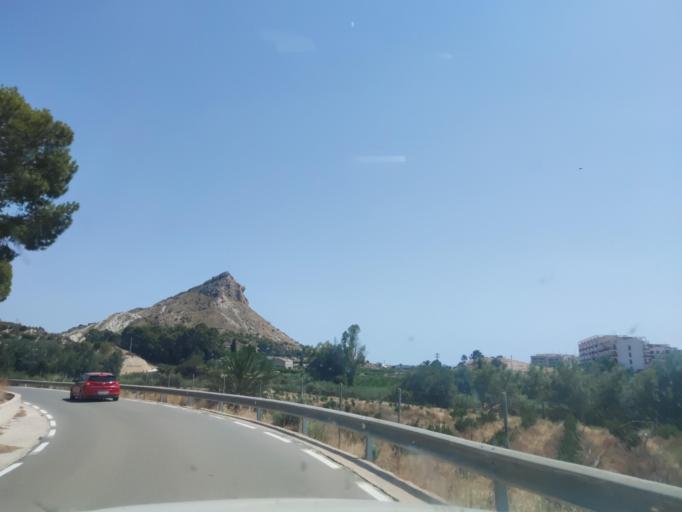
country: ES
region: Murcia
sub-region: Murcia
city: Archena
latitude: 38.1290
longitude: -1.3106
